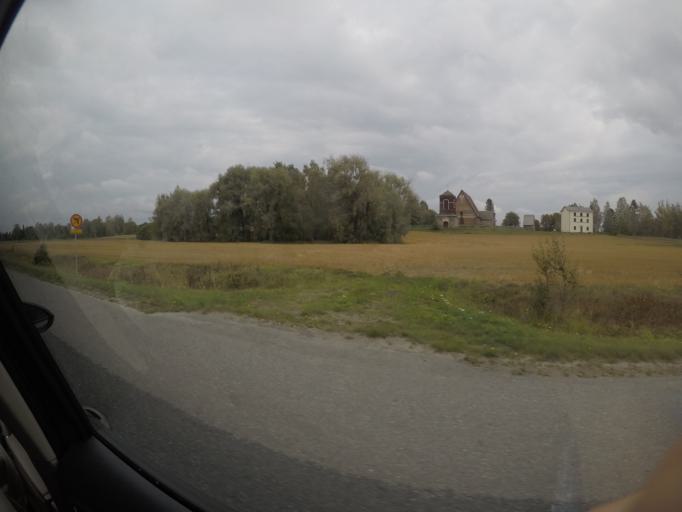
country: FI
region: Haeme
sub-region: Haemeenlinna
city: Parola
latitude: 61.0504
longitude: 24.3950
